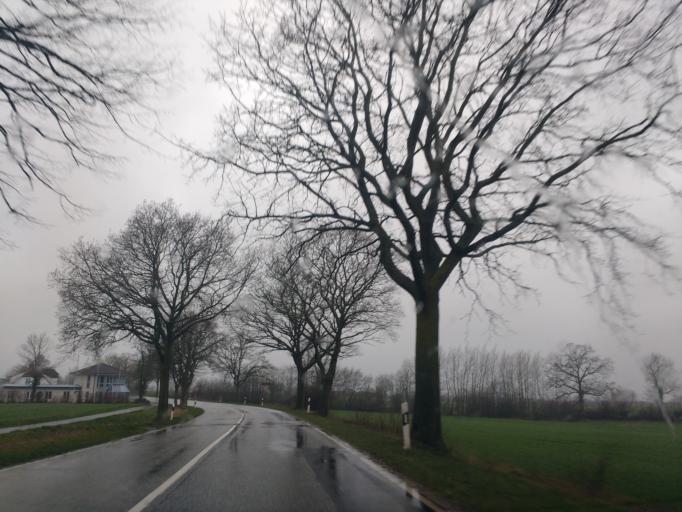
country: DE
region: Schleswig-Holstein
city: Blekendorf
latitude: 54.2835
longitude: 10.6891
